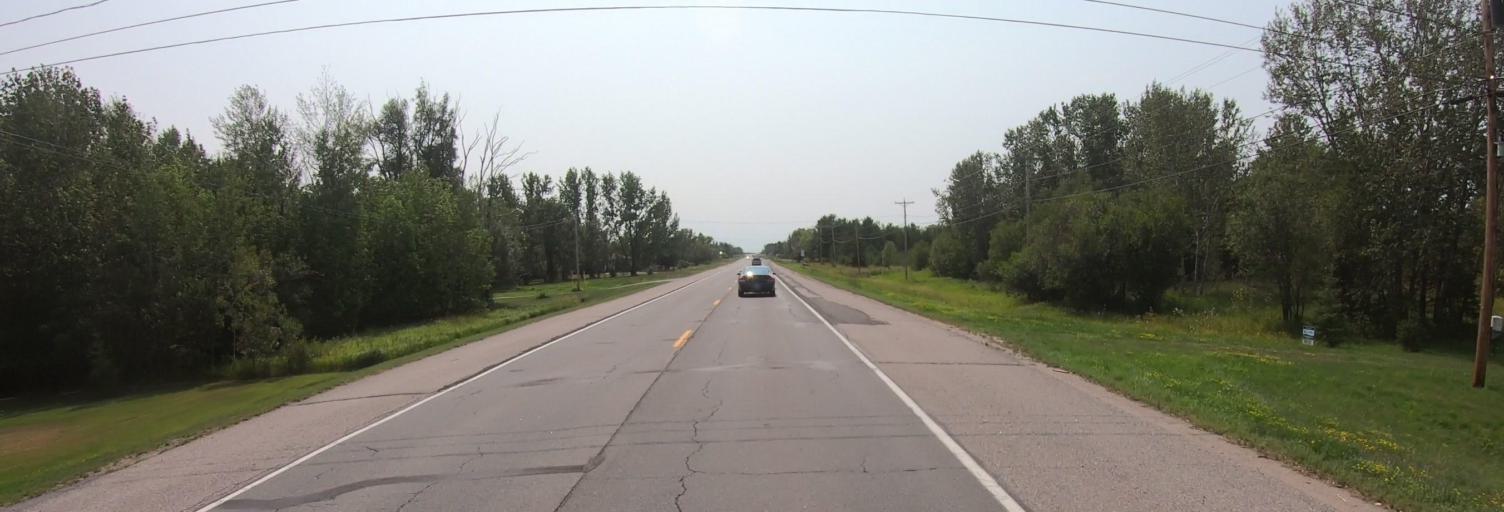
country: US
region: Minnesota
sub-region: Koochiching County
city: International Falls
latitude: 48.5800
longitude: -93.4402
